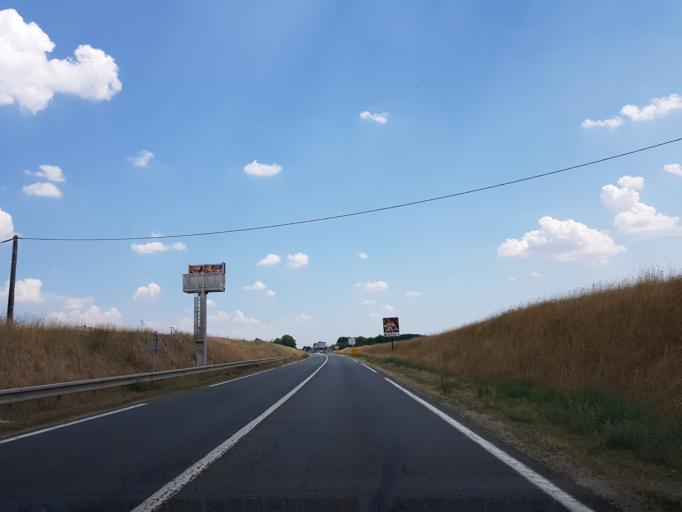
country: FR
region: Centre
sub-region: Departement du Loiret
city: Olivet
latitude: 47.8420
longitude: 1.8969
